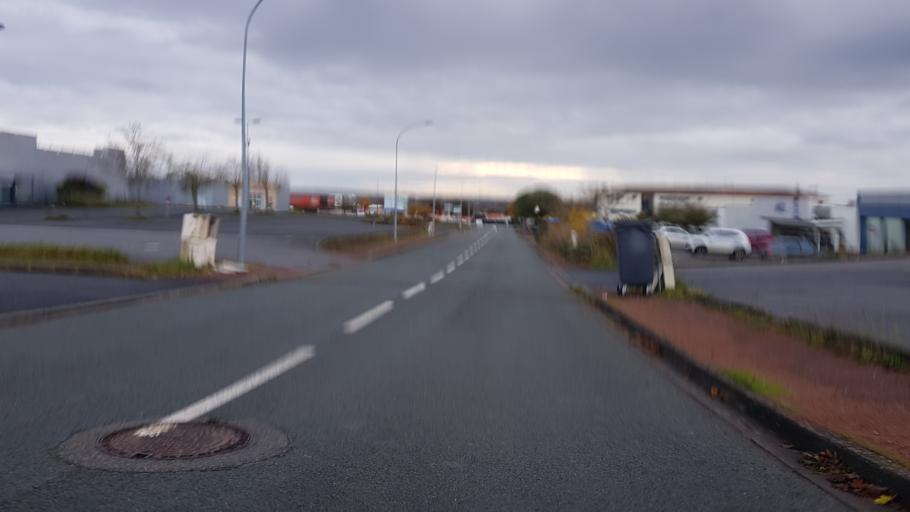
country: FR
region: Poitou-Charentes
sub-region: Departement de la Vienne
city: Chasseneuil-du-Poitou
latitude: 46.6539
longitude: 0.3620
